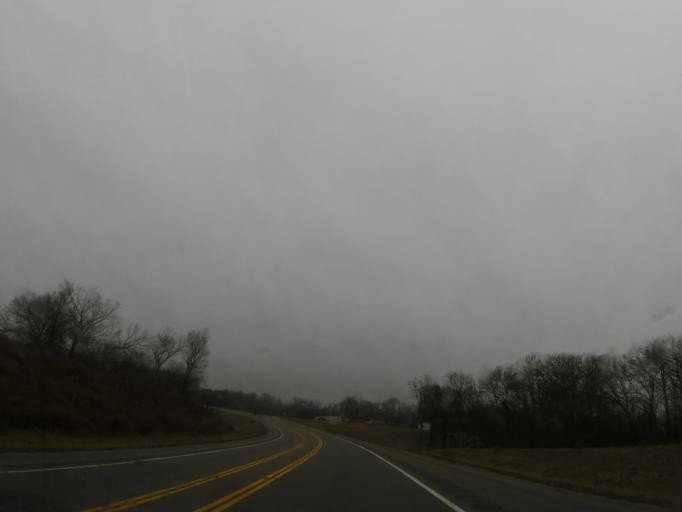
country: US
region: Kentucky
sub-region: Rockcastle County
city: Brodhead
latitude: 37.4587
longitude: -84.5203
